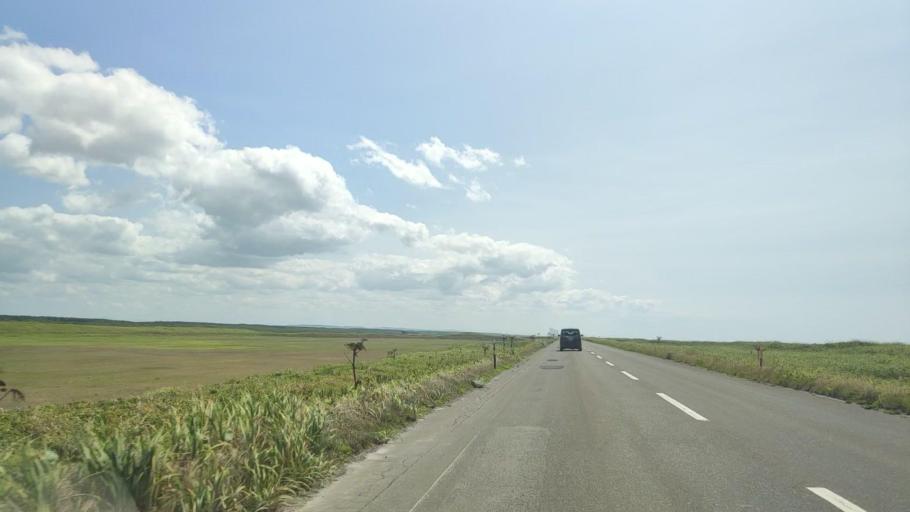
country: JP
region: Hokkaido
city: Makubetsu
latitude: 45.0372
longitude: 141.6610
